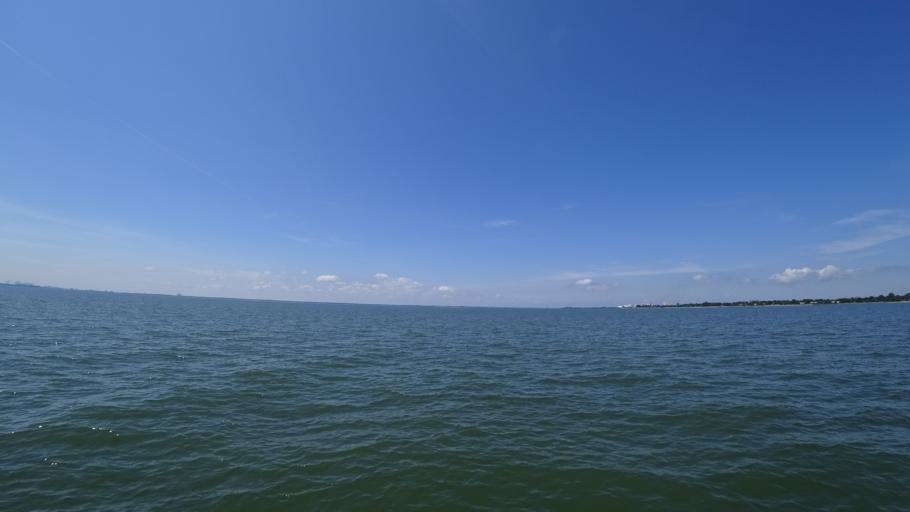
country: US
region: Virginia
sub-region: City of Newport News
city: Newport News
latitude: 36.9833
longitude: -76.3815
